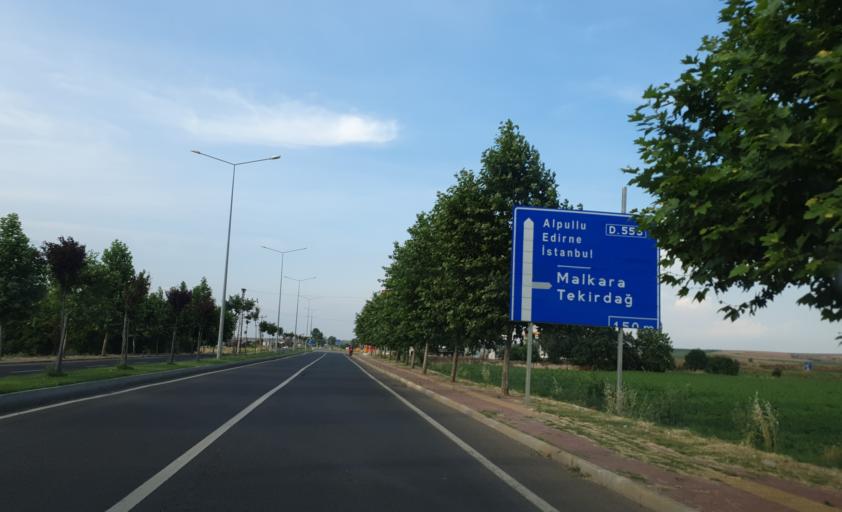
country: TR
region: Tekirdag
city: Hayrabolu
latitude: 41.2239
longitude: 27.1167
